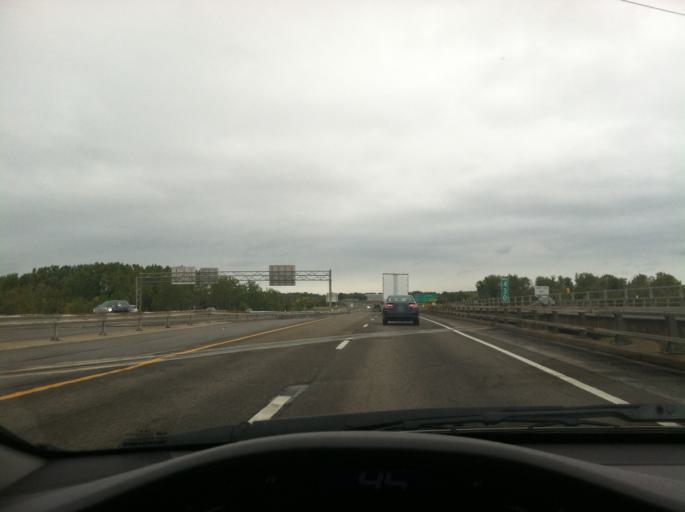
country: US
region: New York
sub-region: Erie County
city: Blasdell
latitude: 42.8097
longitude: -78.8021
